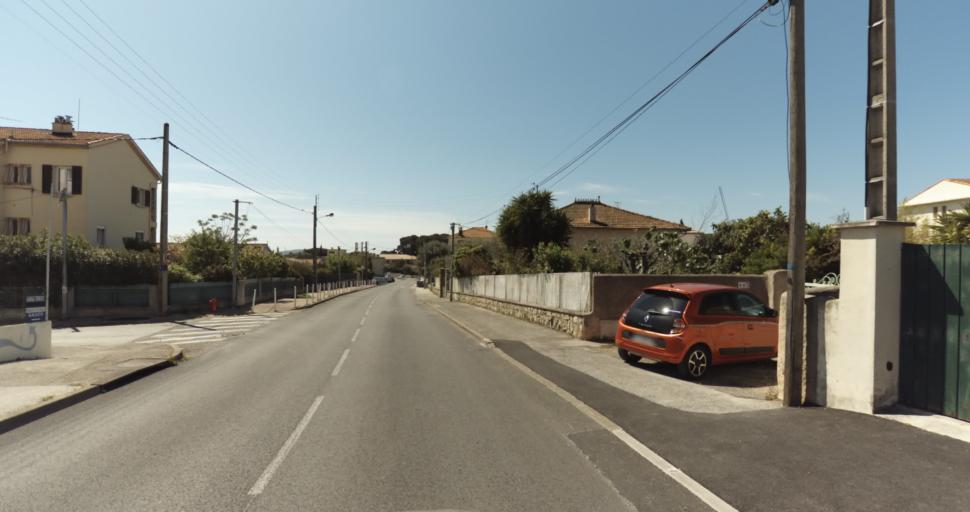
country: FR
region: Provence-Alpes-Cote d'Azur
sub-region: Departement du Var
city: Toulon
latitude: 43.1432
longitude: 5.9016
